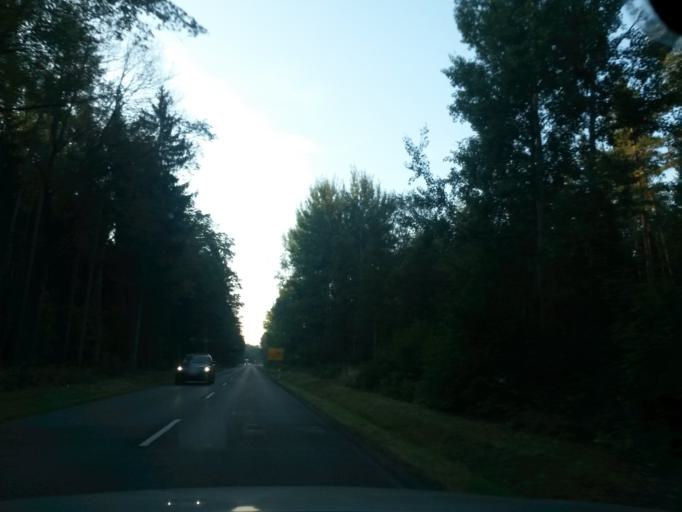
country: DE
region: Thuringia
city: Reichenbach
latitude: 50.8662
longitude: 11.8549
